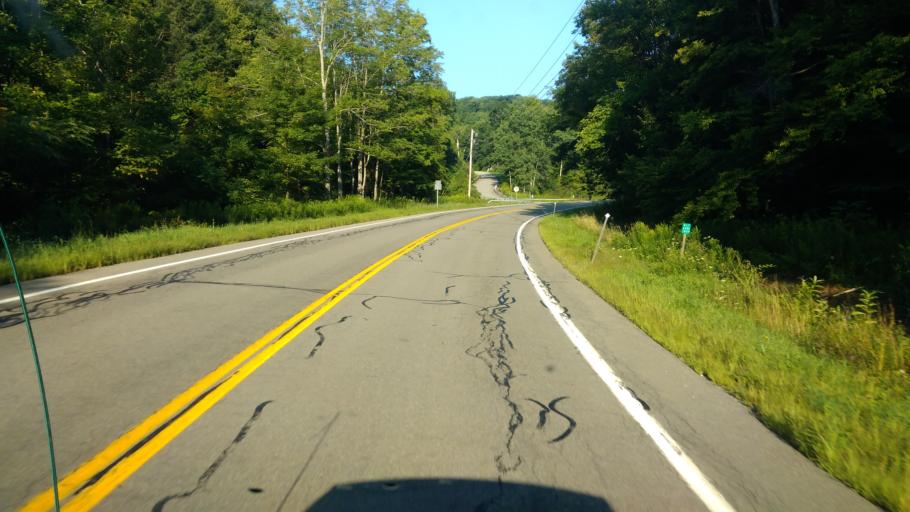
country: US
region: New York
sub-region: Allegany County
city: Andover
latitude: 42.1423
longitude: -77.6771
